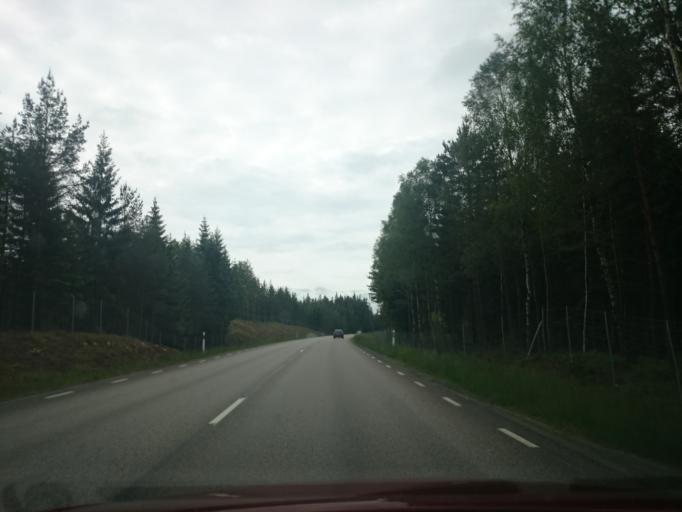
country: SE
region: Vaestra Goetaland
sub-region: Harryda Kommun
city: Hindas
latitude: 57.6862
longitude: 12.3688
